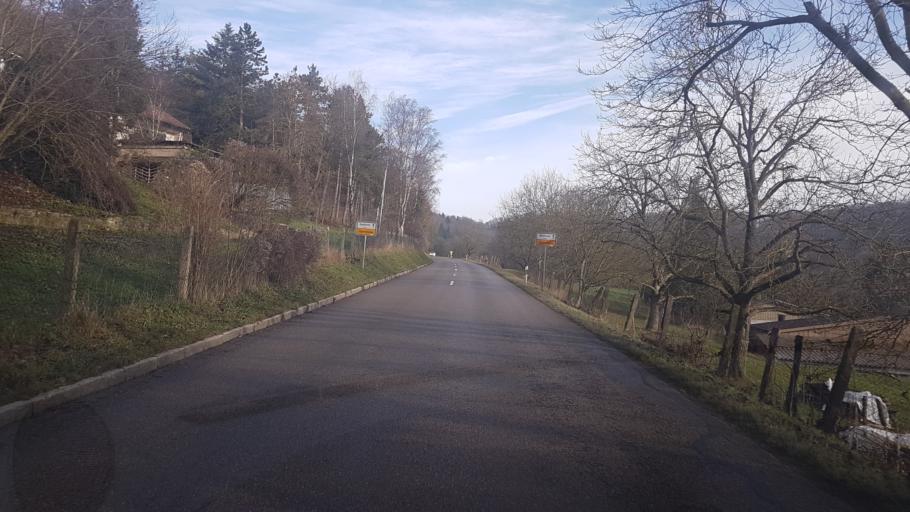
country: DE
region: Baden-Wuerttemberg
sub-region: Regierungsbezirk Stuttgart
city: Ilshofen
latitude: 49.2228
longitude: 9.9030
